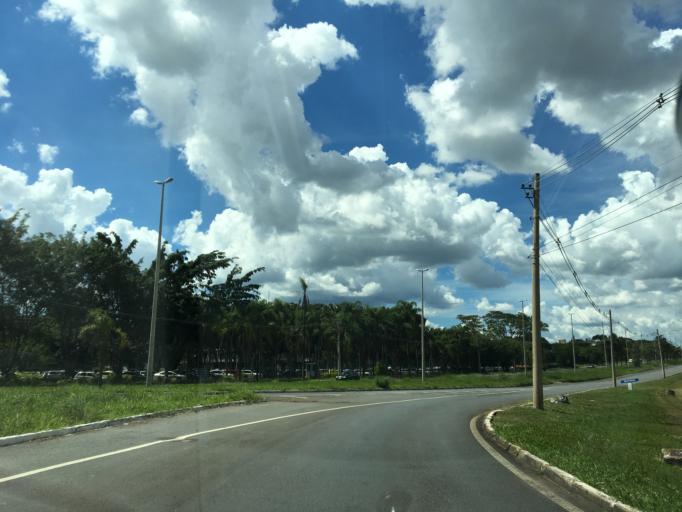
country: BR
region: Federal District
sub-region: Brasilia
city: Brasilia
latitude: -15.7796
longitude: -47.8711
